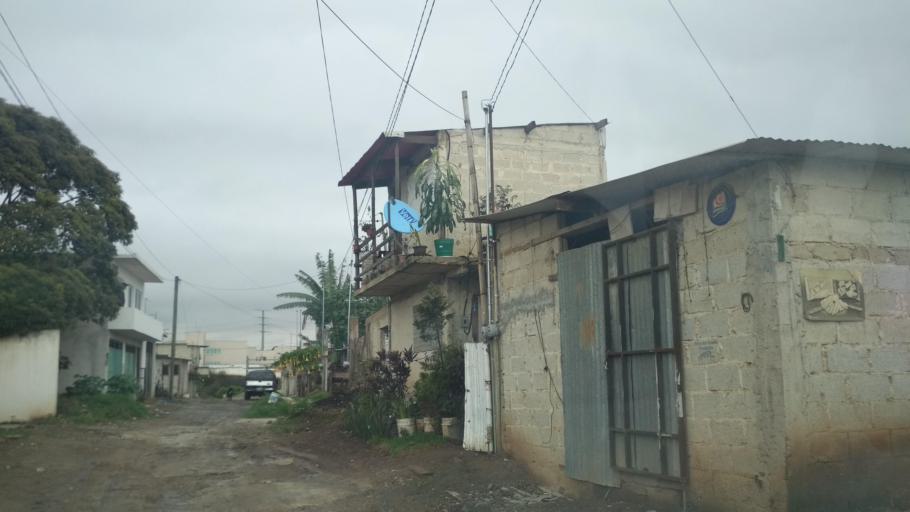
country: MX
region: Veracruz
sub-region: Emiliano Zapata
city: Las Trancas
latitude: 19.5067
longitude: -96.8718
